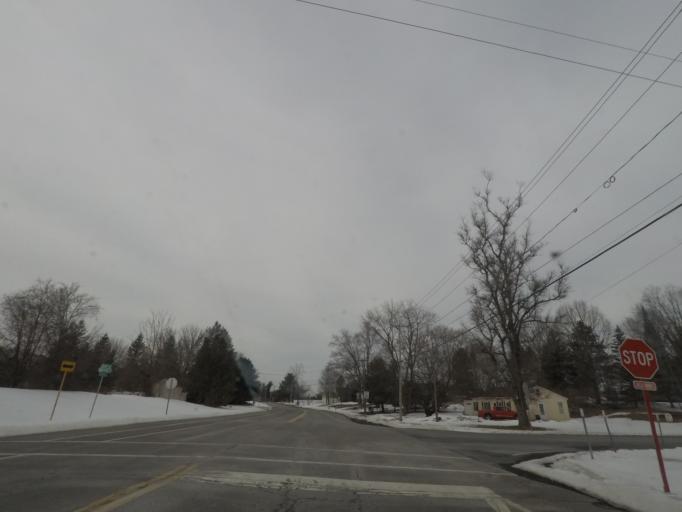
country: US
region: New York
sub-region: Albany County
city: Westmere
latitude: 42.6770
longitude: -73.8944
